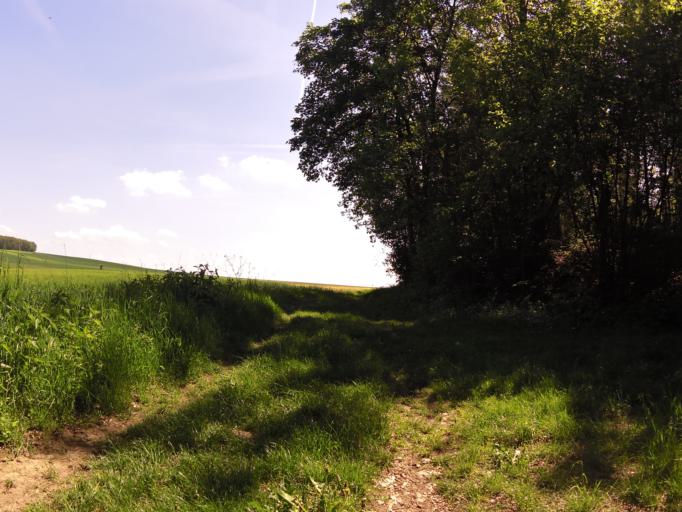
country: DE
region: Bavaria
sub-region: Regierungsbezirk Unterfranken
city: Theilheim
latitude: 49.7398
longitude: 10.0158
